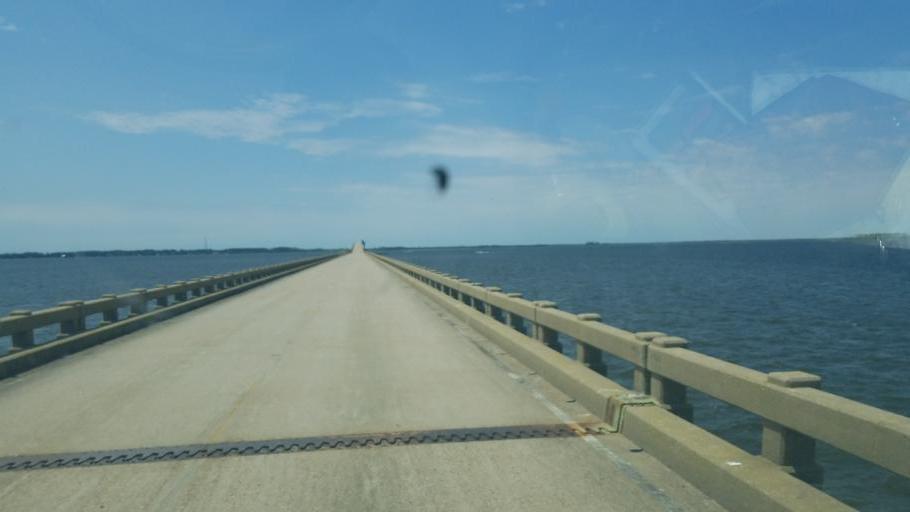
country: US
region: North Carolina
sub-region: Dare County
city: Manteo
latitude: 35.9219
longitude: -75.7394
